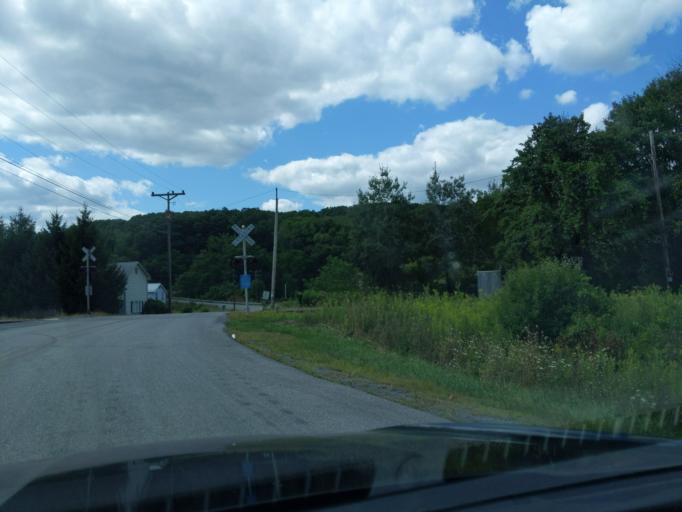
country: US
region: Pennsylvania
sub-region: Blair County
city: Tyrone
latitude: 40.7051
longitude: -78.2131
